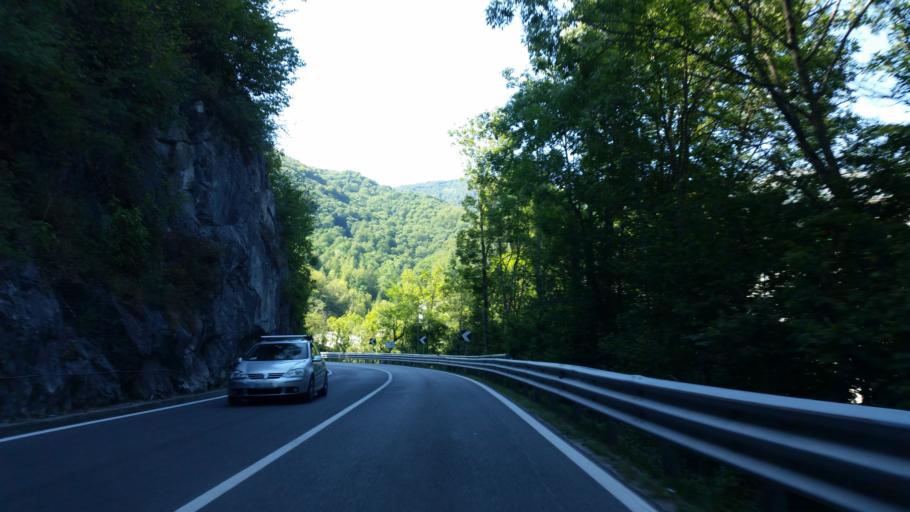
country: IT
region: Piedmont
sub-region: Provincia di Cuneo
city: Vernante
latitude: 44.2626
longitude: 7.5187
